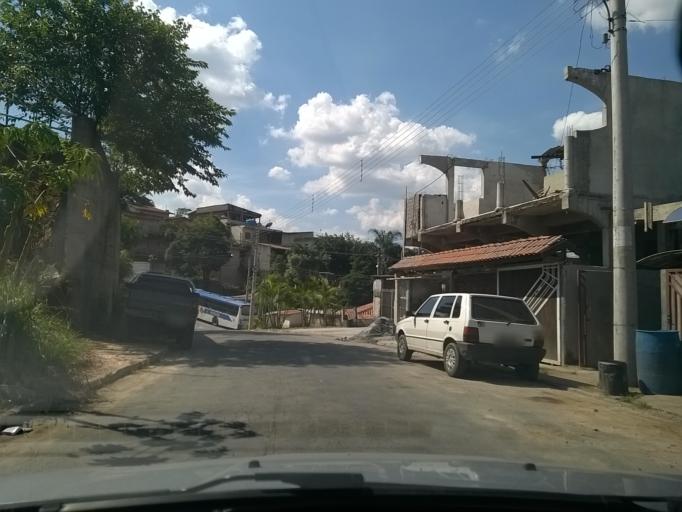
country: BR
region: Sao Paulo
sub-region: Francisco Morato
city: Francisco Morato
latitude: -23.2769
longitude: -46.7447
